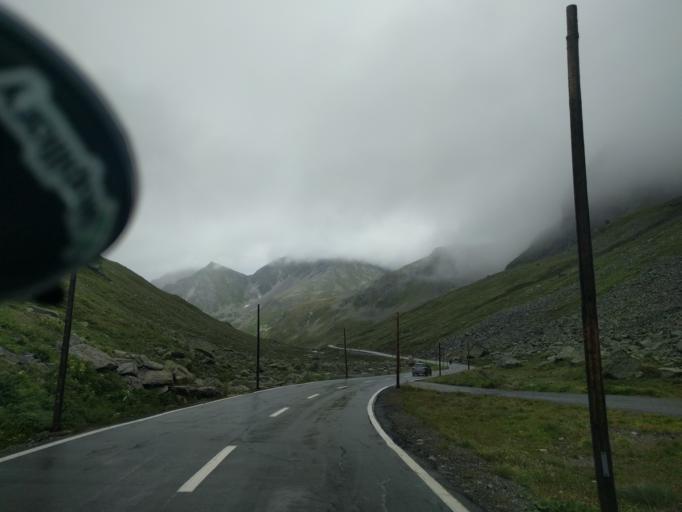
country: CH
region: Grisons
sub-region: Praettigau/Davos District
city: Davos
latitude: 46.7470
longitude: 9.9534
